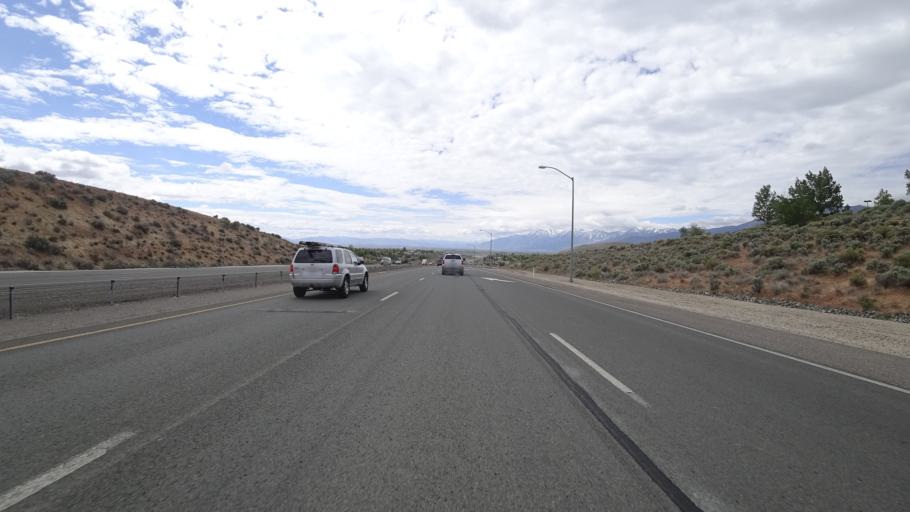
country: US
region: Nevada
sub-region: Douglas County
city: Indian Hills
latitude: 39.0978
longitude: -119.7750
